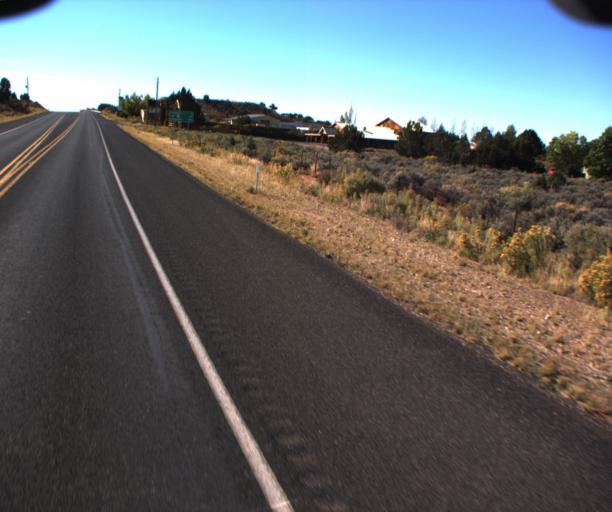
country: US
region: Arizona
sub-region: Coconino County
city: Fredonia
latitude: 36.9956
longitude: -112.5304
